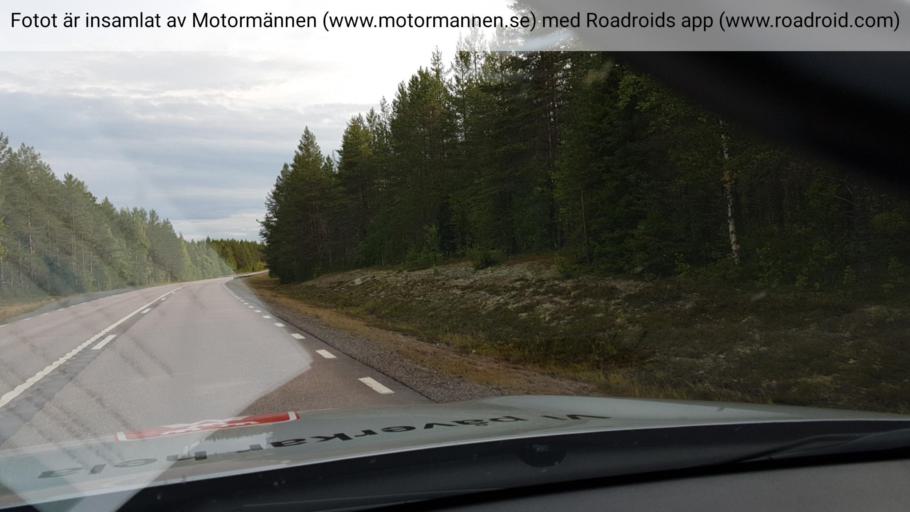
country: SE
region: Norrbotten
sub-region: Kalix Kommun
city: Toere
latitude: 65.9683
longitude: 22.6911
